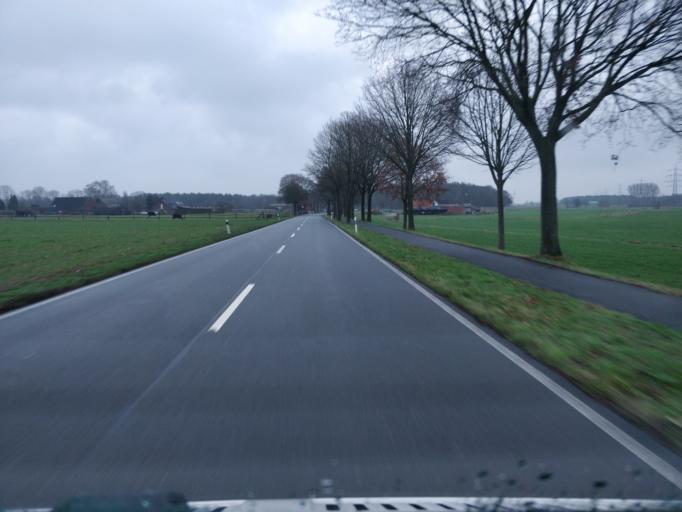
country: DE
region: North Rhine-Westphalia
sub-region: Regierungsbezirk Dusseldorf
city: Mehrhoog
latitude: 51.7586
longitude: 6.5198
